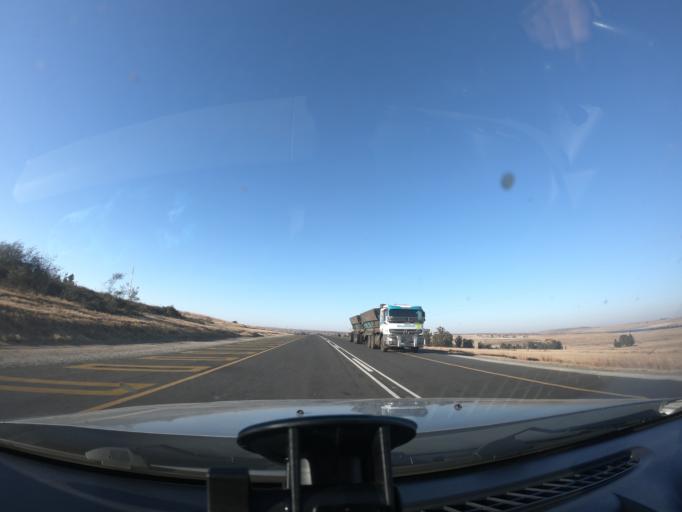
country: ZA
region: Mpumalanga
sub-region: Gert Sibande District Municipality
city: Ermelo
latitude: -26.4406
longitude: 29.9472
